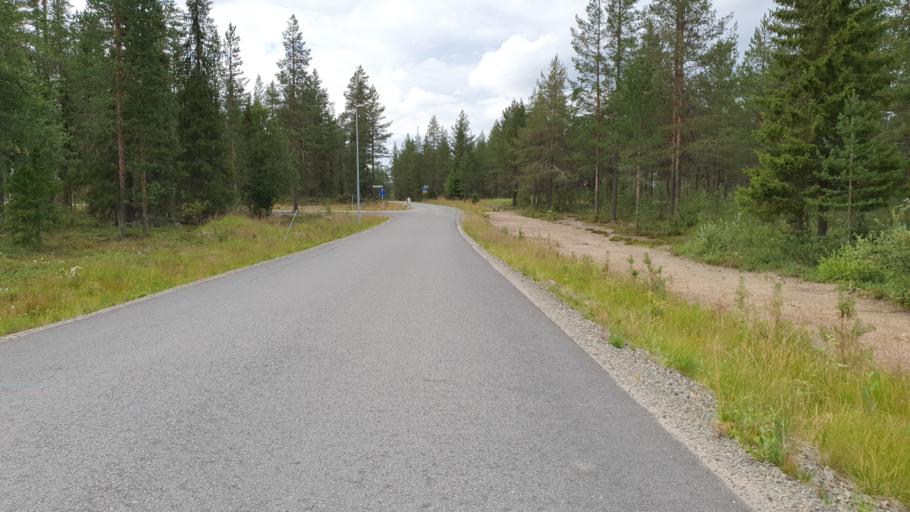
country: FI
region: Lapland
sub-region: Tunturi-Lappi
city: Kolari
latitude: 67.5982
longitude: 24.1383
